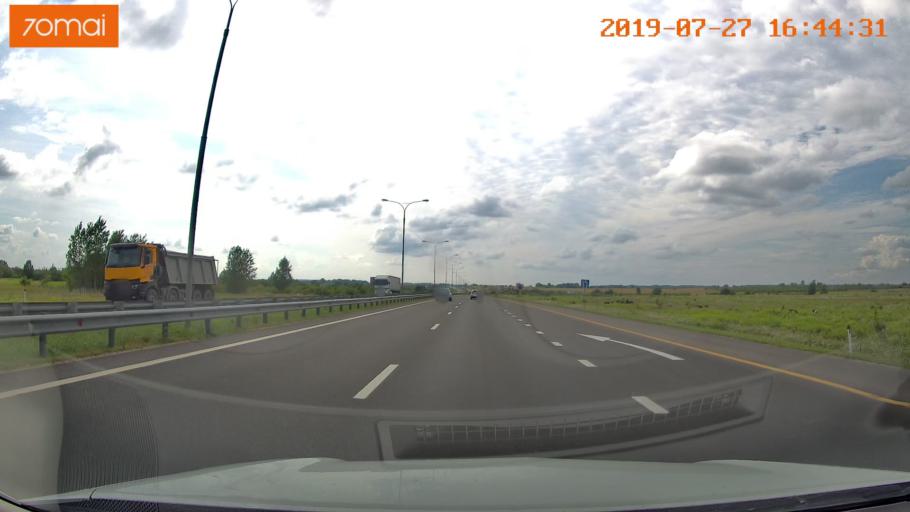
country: RU
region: Kaliningrad
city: Gvardeysk
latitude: 54.6723
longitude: 21.0768
